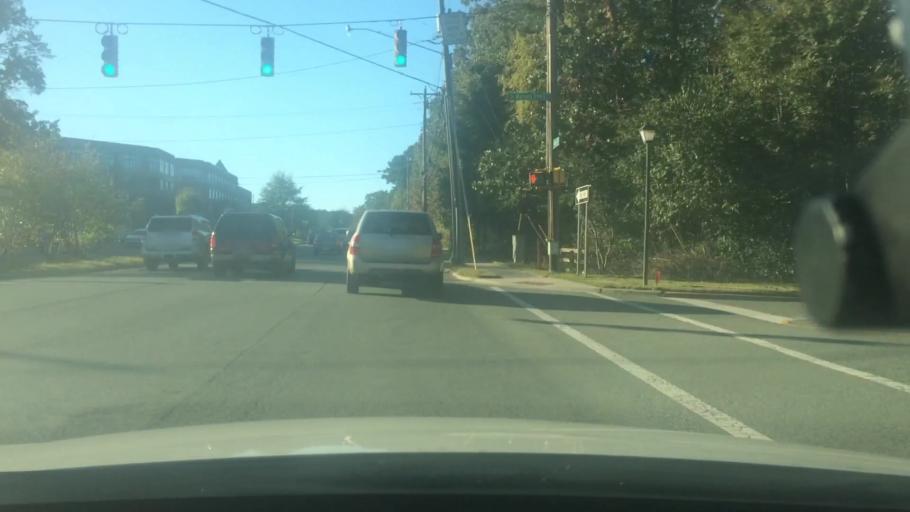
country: US
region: North Carolina
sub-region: Orange County
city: Chapel Hill
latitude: 35.9064
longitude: -79.0187
